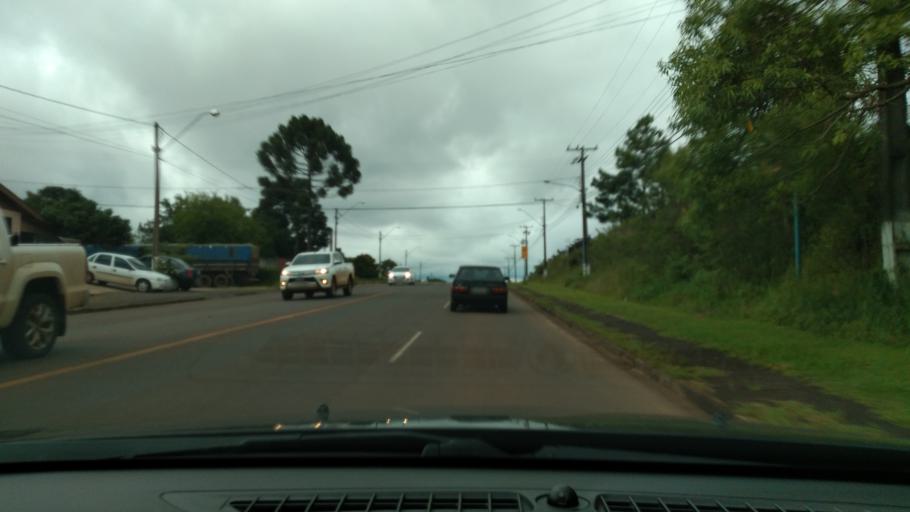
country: BR
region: Parana
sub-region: Guarapuava
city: Guarapuava
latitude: -25.3937
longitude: -51.4880
